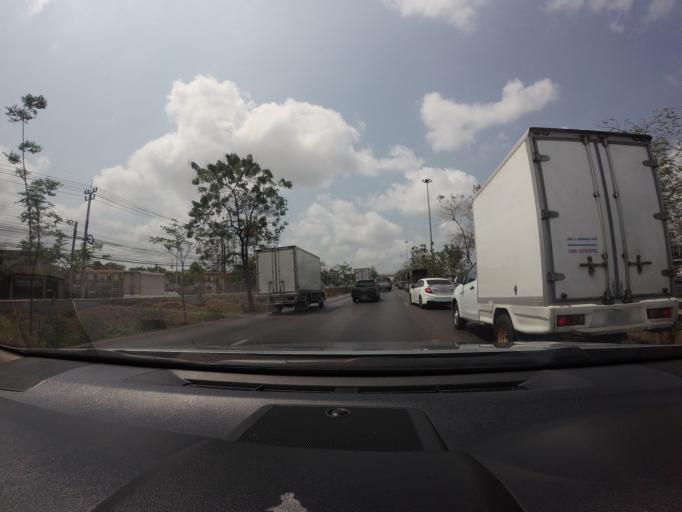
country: TH
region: Bangkok
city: Bang Bon
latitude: 13.6232
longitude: 100.3906
